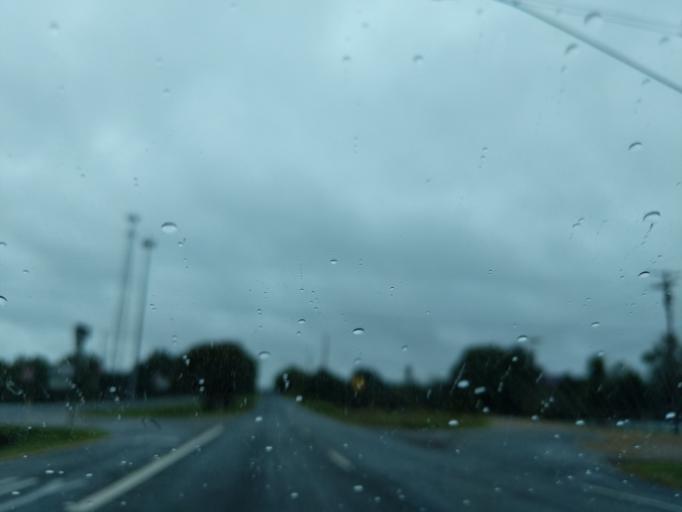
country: US
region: Texas
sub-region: Nacogdoches County
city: Nacogdoches
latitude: 31.6602
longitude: -94.6585
